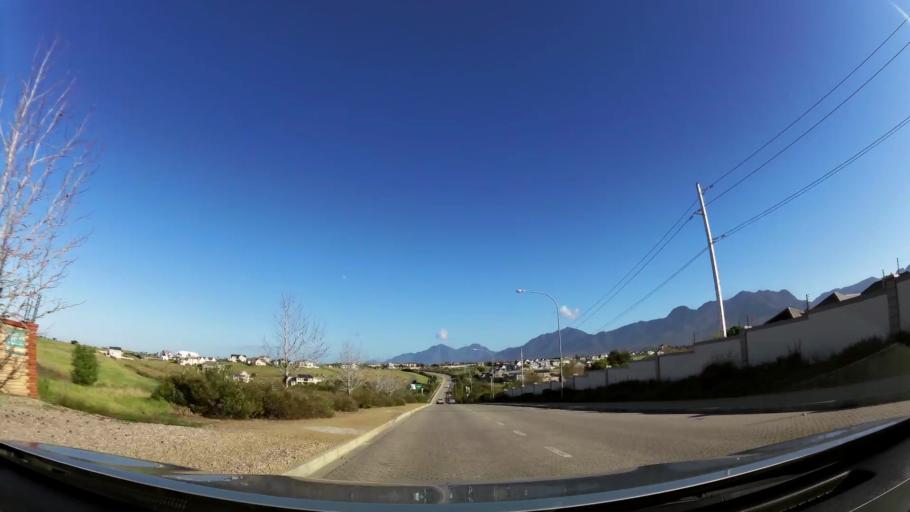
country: ZA
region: Western Cape
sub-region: Eden District Municipality
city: George
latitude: -33.9673
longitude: 22.4373
